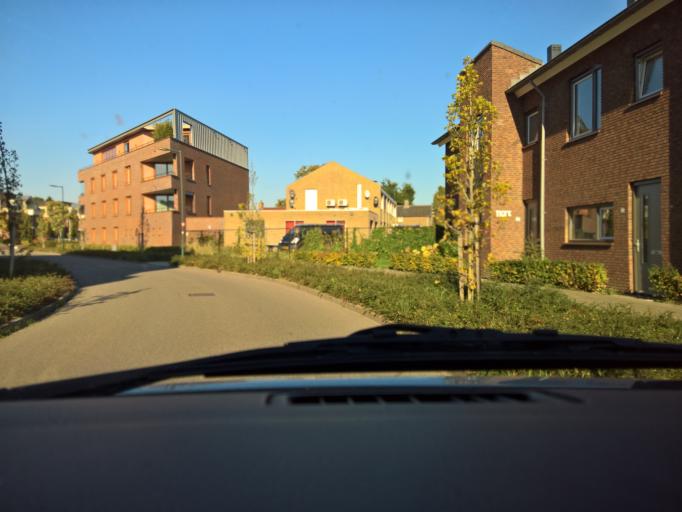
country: NL
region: Gelderland
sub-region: Gemeente Beuningen
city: Beuningen
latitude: 51.8620
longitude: 5.7734
